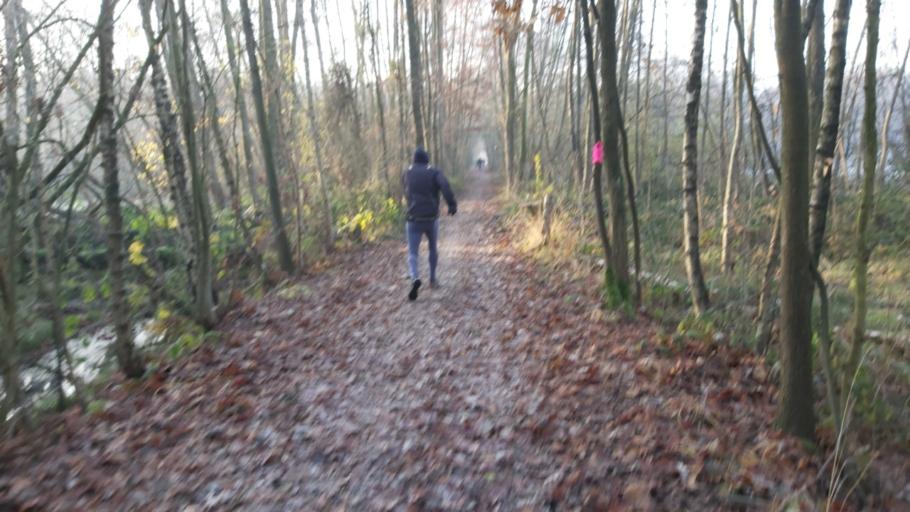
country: BE
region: Flanders
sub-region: Provincie Limburg
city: Lummen
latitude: 50.9830
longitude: 5.2333
